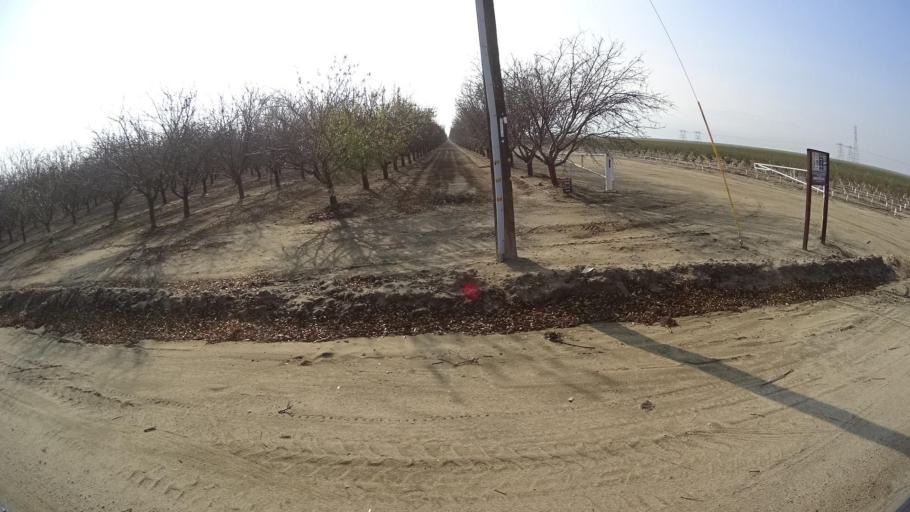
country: US
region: California
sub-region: Kern County
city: Lebec
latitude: 34.9930
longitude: -118.8554
